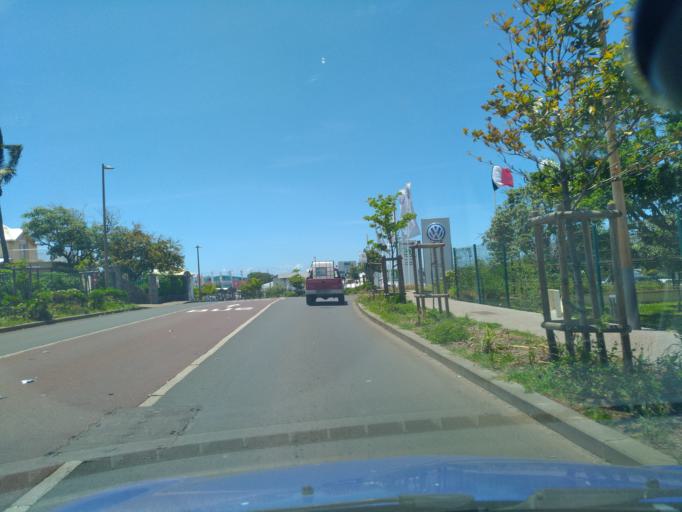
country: RE
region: Reunion
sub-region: Reunion
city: Saint-Pierre
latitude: -21.3324
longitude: 55.4560
